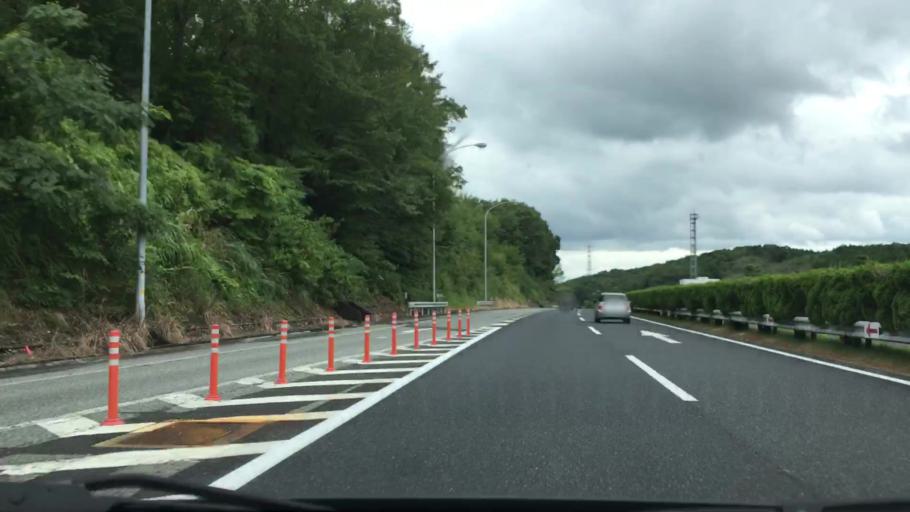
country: JP
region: Okayama
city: Tsuyama
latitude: 35.0444
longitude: 134.1033
